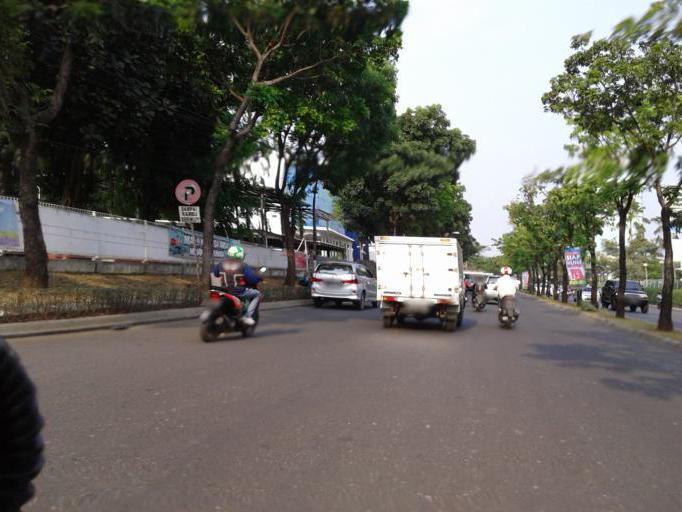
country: ID
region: Banten
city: South Tangerang
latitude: -6.2787
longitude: 106.7207
